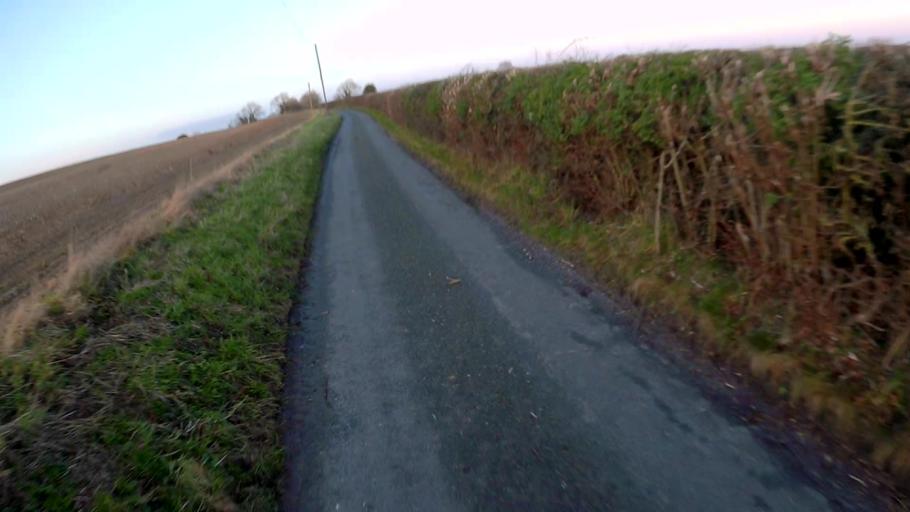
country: GB
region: England
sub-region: Hampshire
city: Overton
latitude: 51.2251
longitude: -1.2396
